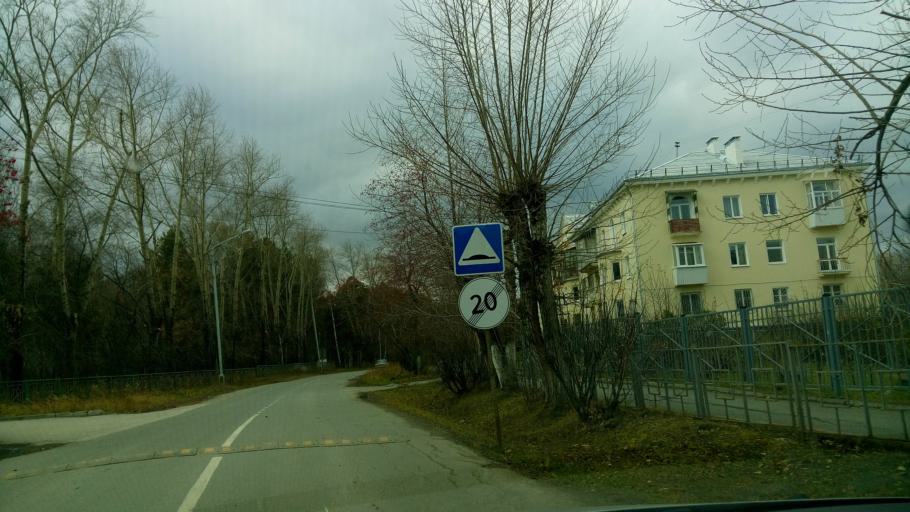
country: RU
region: Sverdlovsk
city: Sredneuralsk
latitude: 56.9896
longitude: 60.4708
